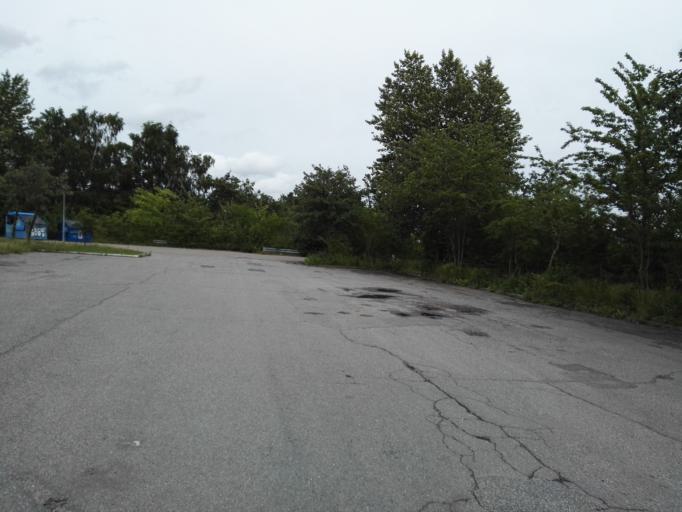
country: DK
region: Capital Region
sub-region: Egedal Kommune
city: Olstykke
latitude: 55.7722
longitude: 12.1672
